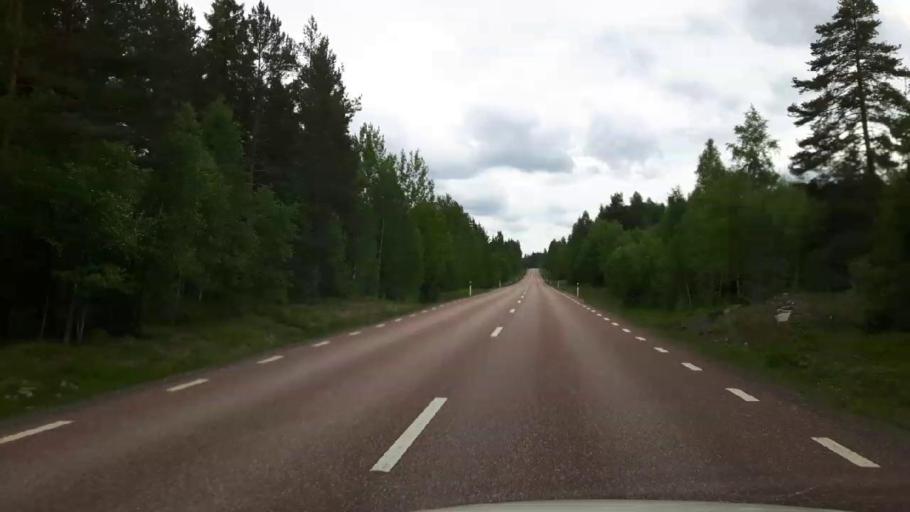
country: SE
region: Dalarna
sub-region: Hedemora Kommun
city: Brunna
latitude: 60.2007
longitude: 15.9946
